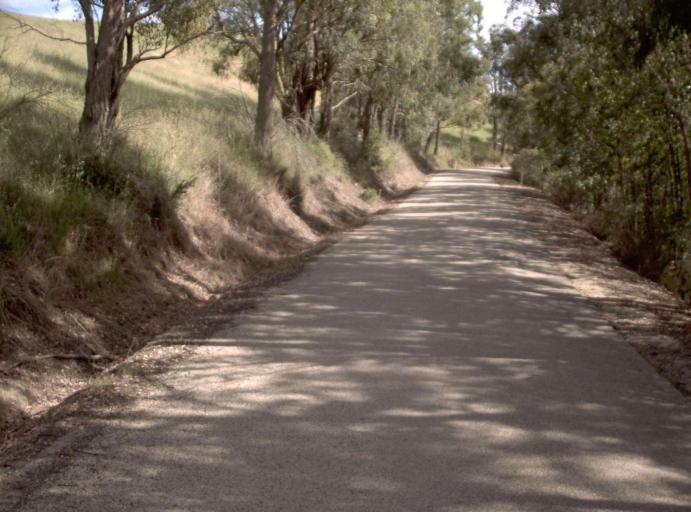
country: AU
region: Victoria
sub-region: East Gippsland
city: Lakes Entrance
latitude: -37.5157
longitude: 148.1414
